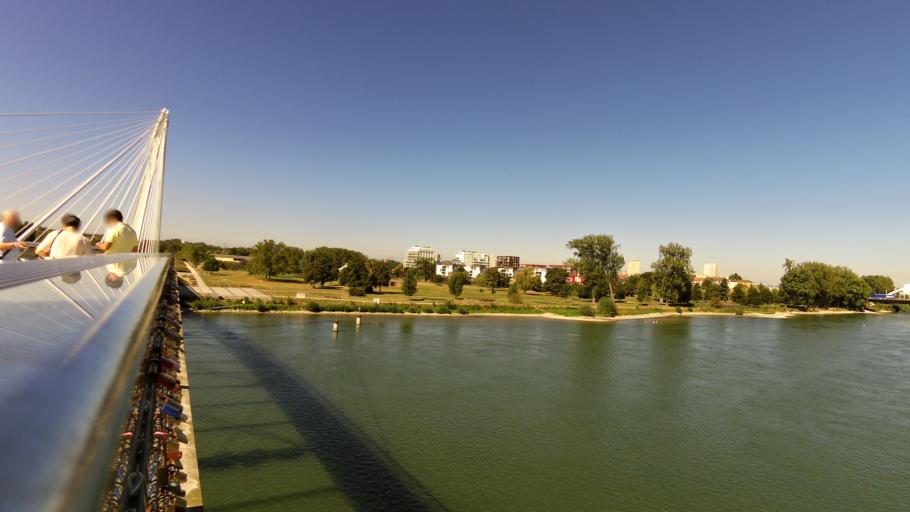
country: DE
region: Baden-Wuerttemberg
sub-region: Freiburg Region
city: Kehl
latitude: 48.5692
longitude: 7.8037
